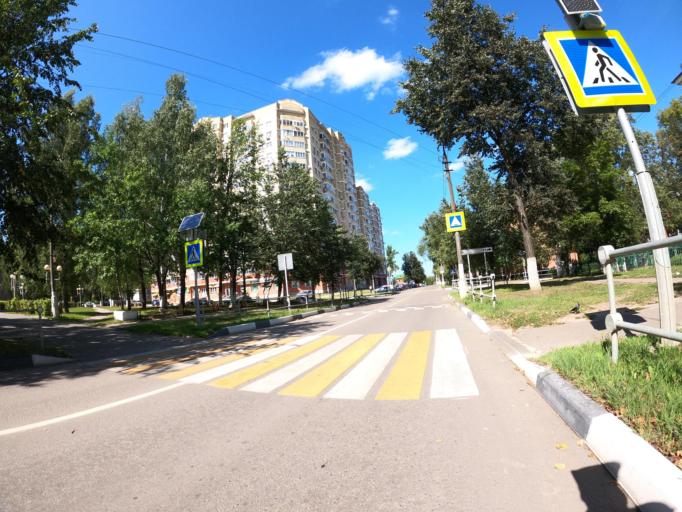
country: RU
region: Moskovskaya
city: Stupino
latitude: 54.8874
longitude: 38.0874
